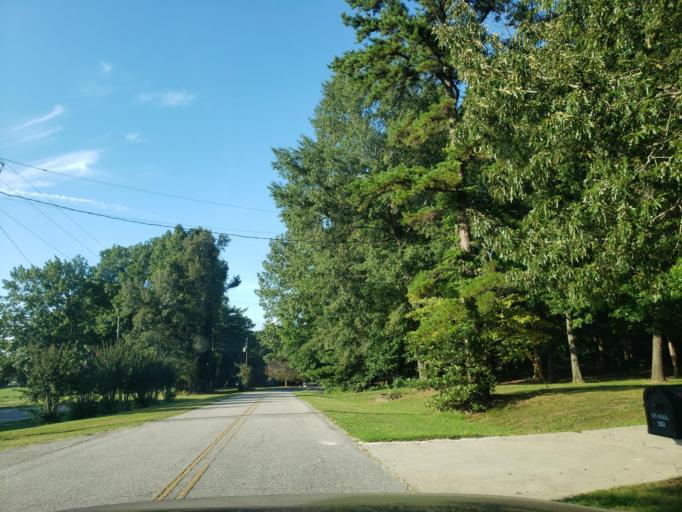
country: US
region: North Carolina
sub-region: Vance County
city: Henderson
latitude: 36.4043
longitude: -78.3760
